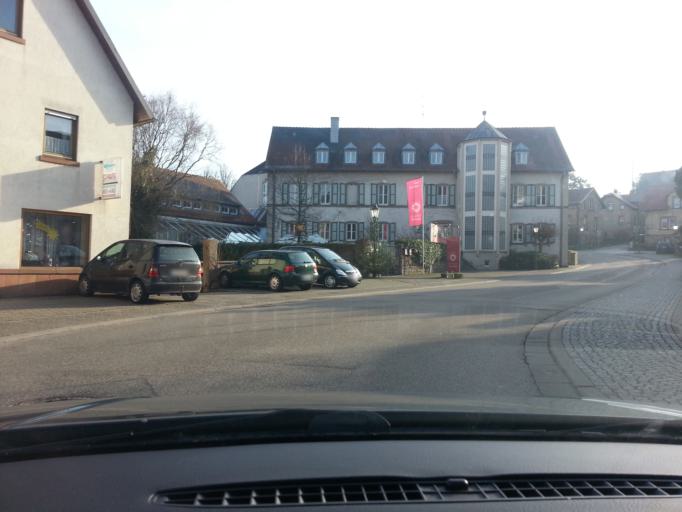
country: DE
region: Rheinland-Pfalz
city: Klingenmunster
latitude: 49.1401
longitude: 8.0197
